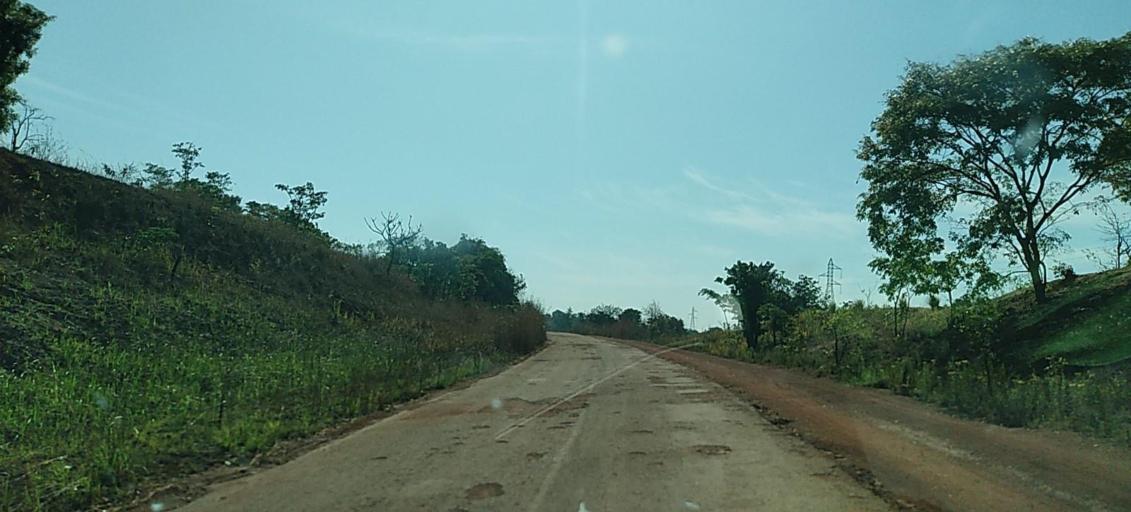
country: ZM
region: North-Western
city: Mwinilunga
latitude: -11.8259
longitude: 25.1272
